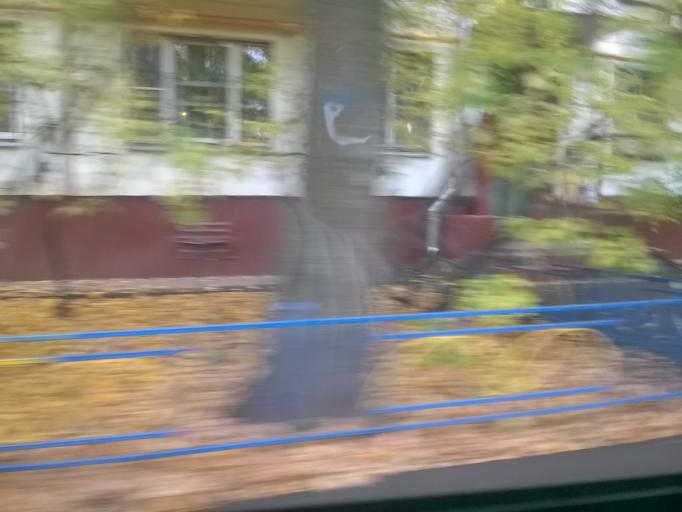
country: RU
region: Moscow
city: Nikol'skoye
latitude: 55.6766
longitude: 37.4919
